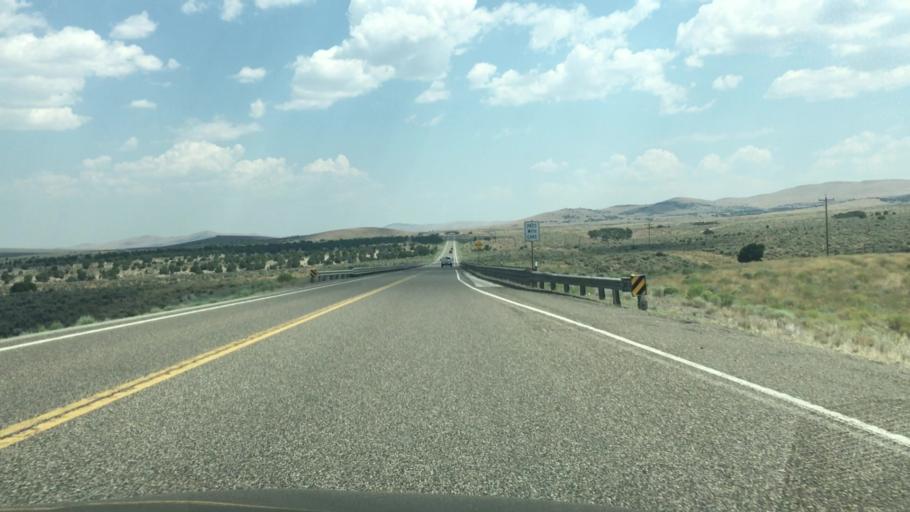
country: US
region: Nevada
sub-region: Elko County
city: Wells
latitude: 41.1941
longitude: -114.8672
